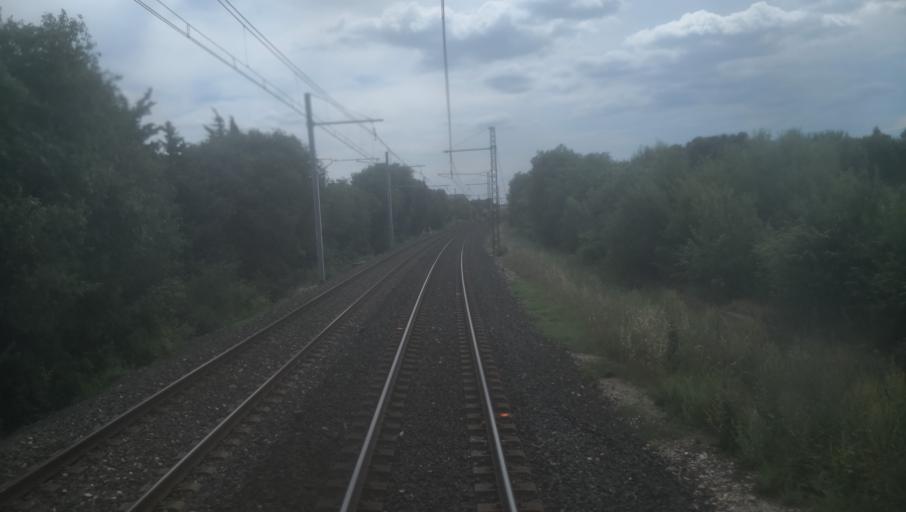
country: FR
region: Languedoc-Roussillon
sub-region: Departement du Gard
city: Uchaud
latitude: 43.7603
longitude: 4.2715
